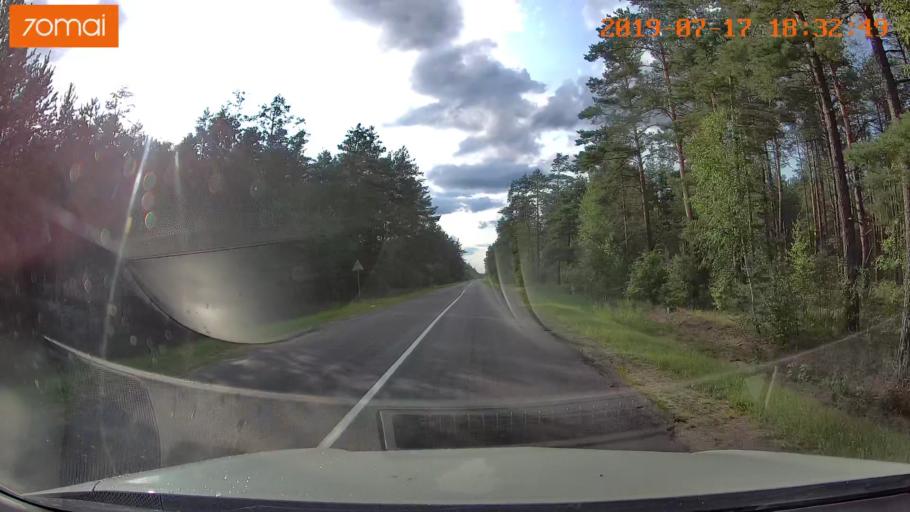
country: BY
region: Mogilev
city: Asipovichy
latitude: 53.2747
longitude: 28.6737
